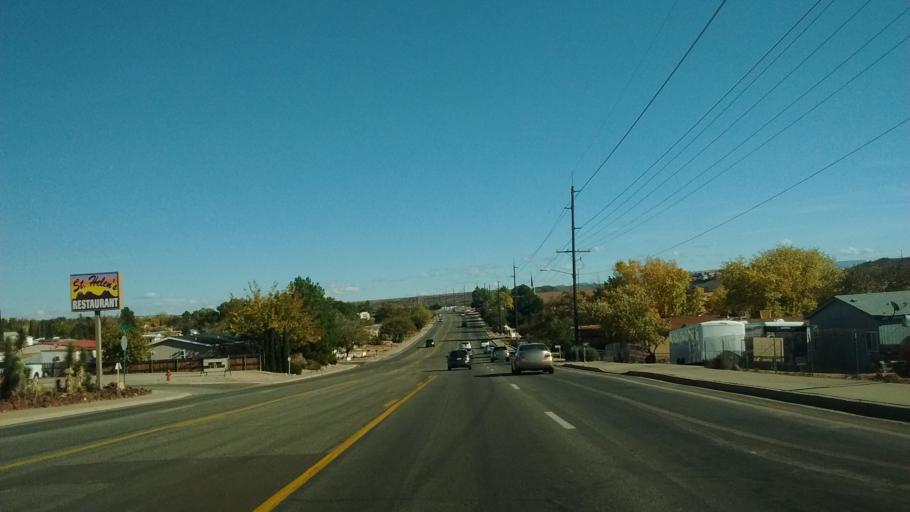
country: US
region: Utah
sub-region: Washington County
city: Washington
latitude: 37.1302
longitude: -113.5040
